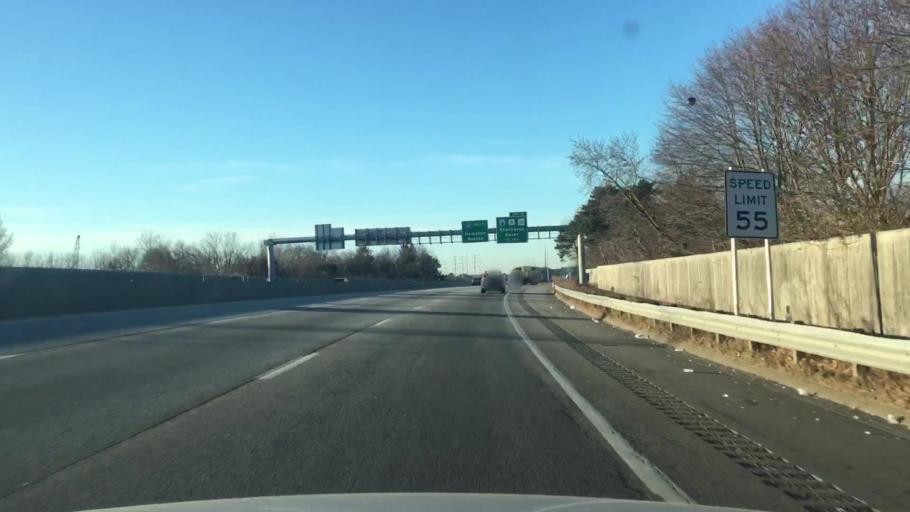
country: US
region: New Hampshire
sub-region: Rockingham County
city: Portsmouth
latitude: 43.0784
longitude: -70.7769
